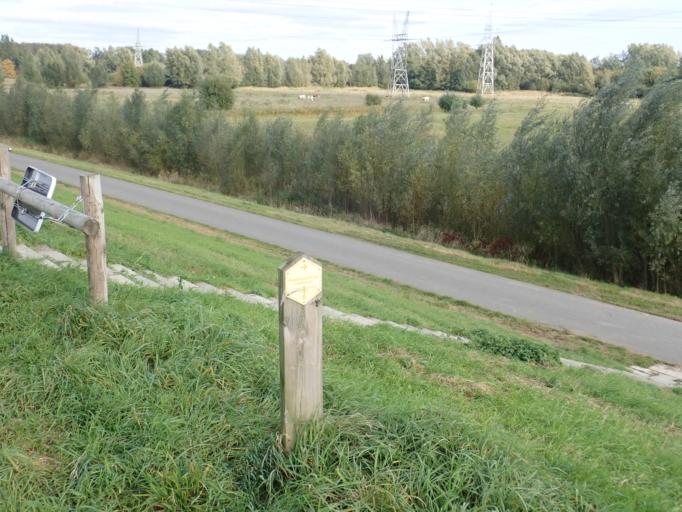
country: BE
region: Flanders
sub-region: Provincie Antwerpen
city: Niel
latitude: 51.1301
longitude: 4.2996
